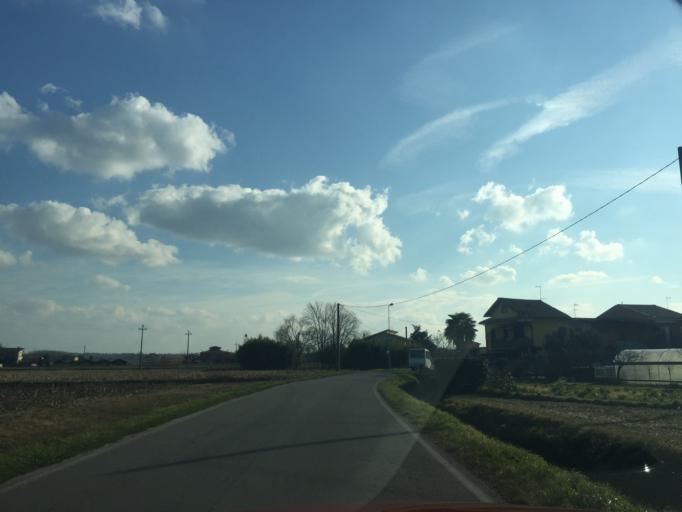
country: IT
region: Tuscany
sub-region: Provincia di Pistoia
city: Anchione
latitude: 43.8292
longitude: 10.7423
